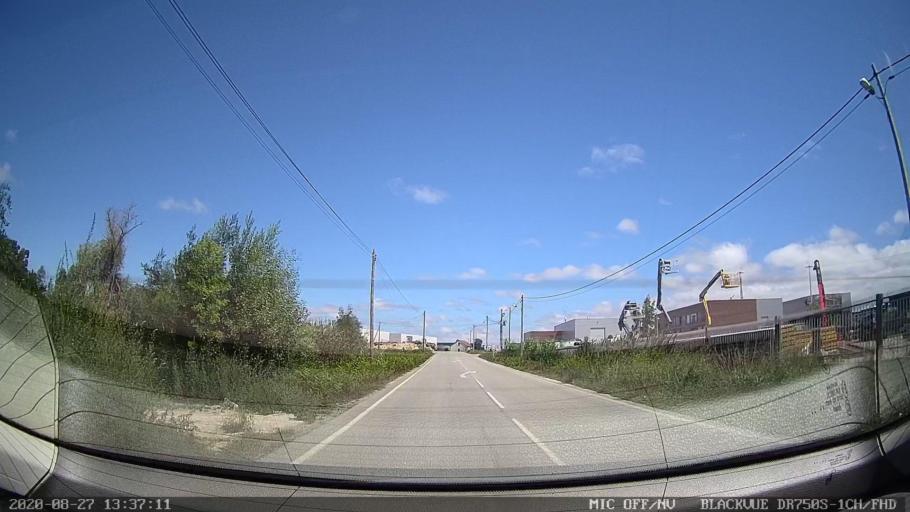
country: PT
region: Coimbra
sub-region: Mira
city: Mira
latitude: 40.4546
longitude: -8.7114
